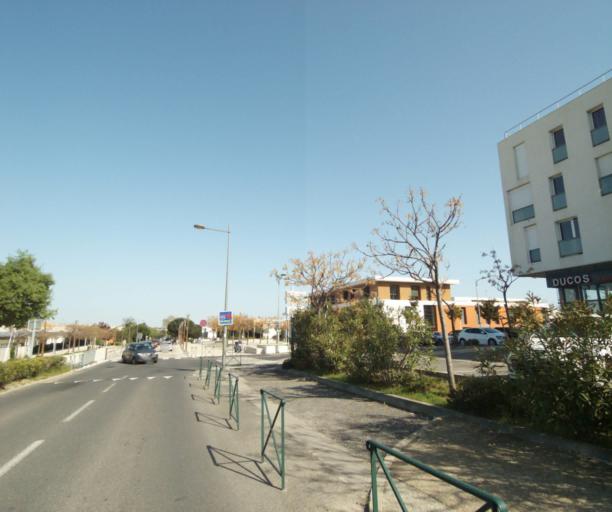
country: FR
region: Languedoc-Roussillon
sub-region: Departement de l'Herault
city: Juvignac
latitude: 43.6140
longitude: 3.8041
